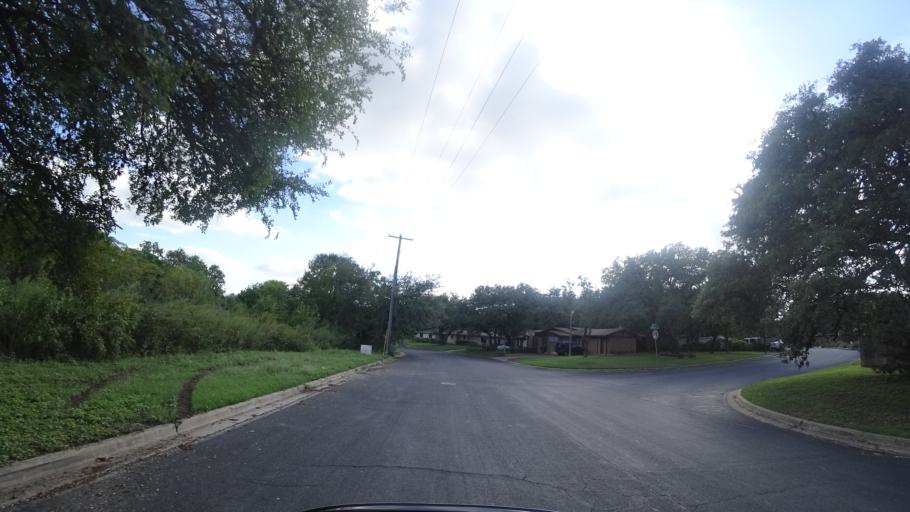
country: US
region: Texas
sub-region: Travis County
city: Rollingwood
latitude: 30.2110
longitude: -97.7897
